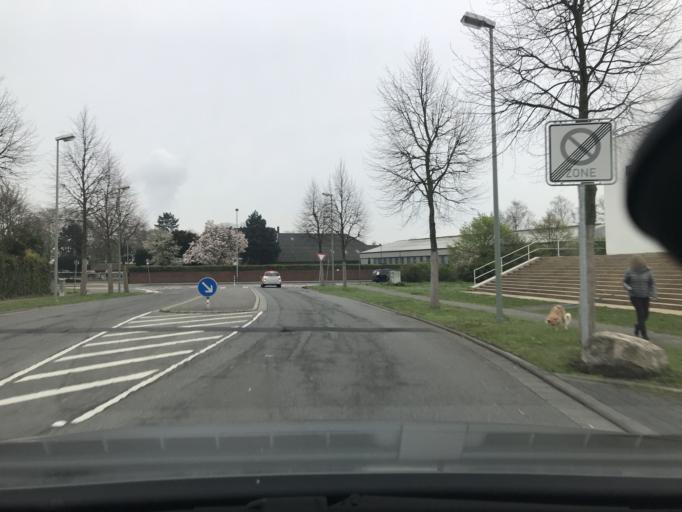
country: DE
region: North Rhine-Westphalia
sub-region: Regierungsbezirk Dusseldorf
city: Krefeld
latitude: 51.3689
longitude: 6.6399
